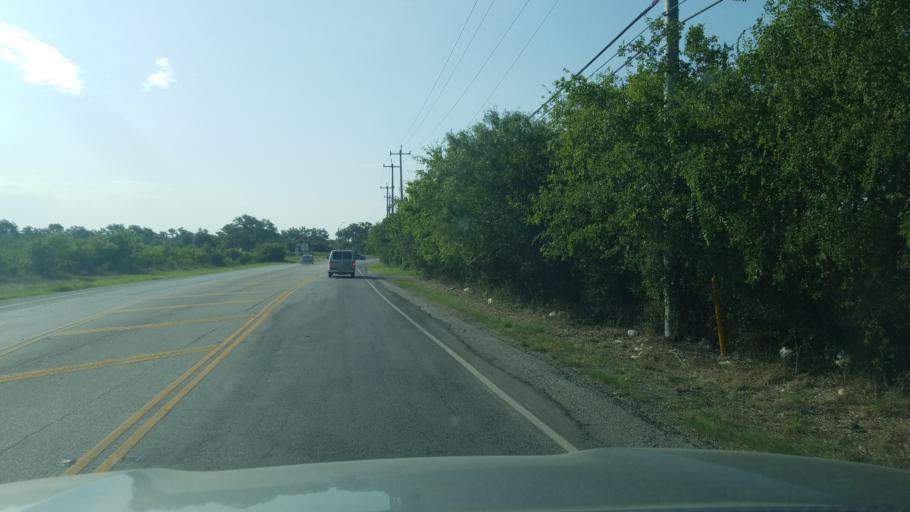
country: US
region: Texas
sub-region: Bexar County
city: Helotes
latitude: 29.4624
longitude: -98.7599
